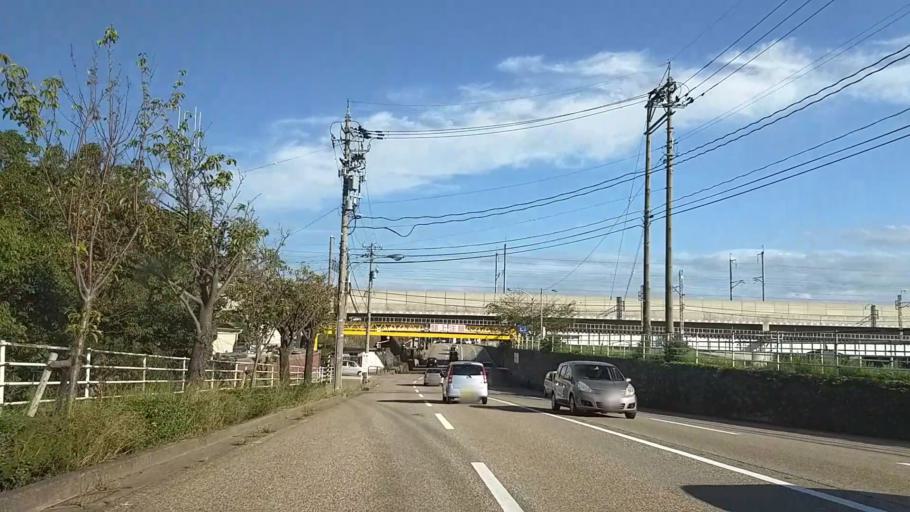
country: JP
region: Ishikawa
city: Kanazawa-shi
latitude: 36.5680
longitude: 136.6389
